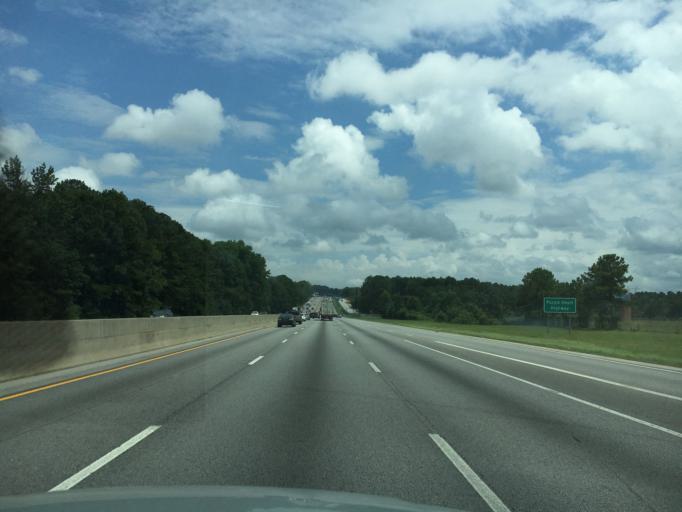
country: US
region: Georgia
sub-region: DeKalb County
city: Lithonia
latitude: 33.6980
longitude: -84.0841
